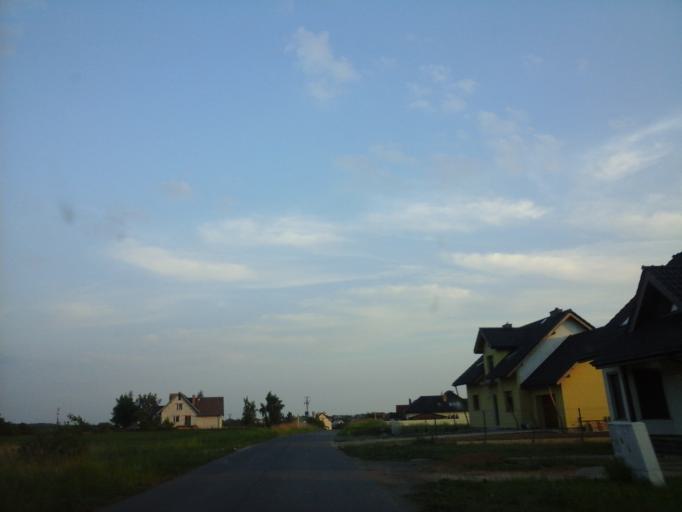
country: PL
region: West Pomeranian Voivodeship
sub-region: Powiat choszczenski
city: Choszczno
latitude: 53.1845
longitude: 15.4157
